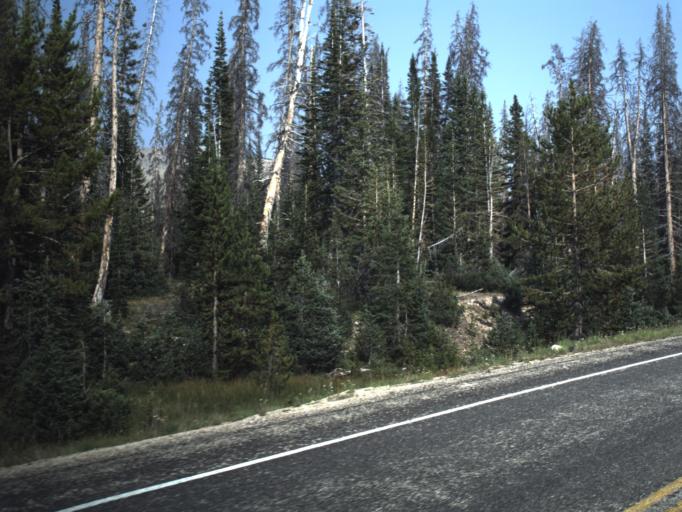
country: US
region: Utah
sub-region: Summit County
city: Kamas
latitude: 40.6846
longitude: -110.9298
